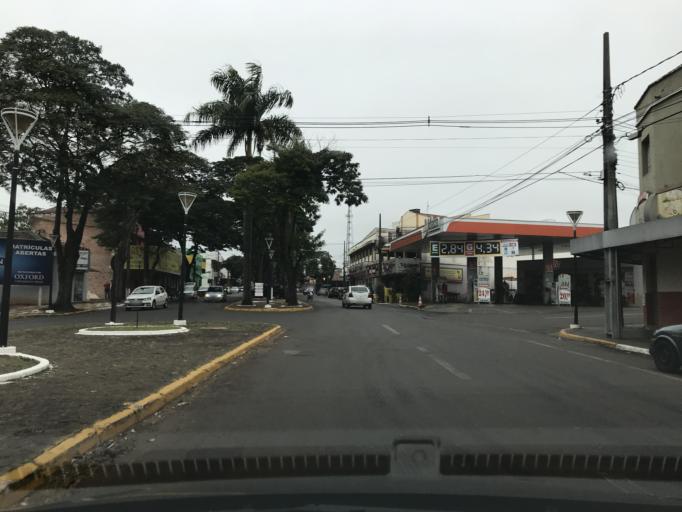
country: PY
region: Canindeyu
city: Salto del Guaira
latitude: -24.0823
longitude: -54.2492
